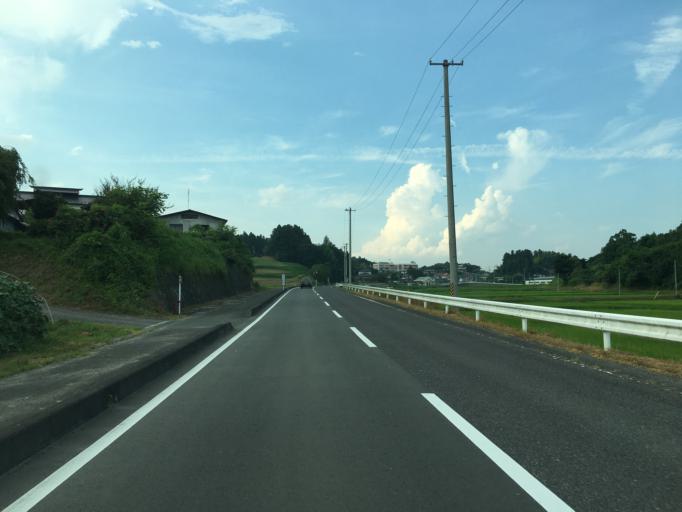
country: JP
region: Fukushima
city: Motomiya
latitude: 37.5201
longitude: 140.4440
